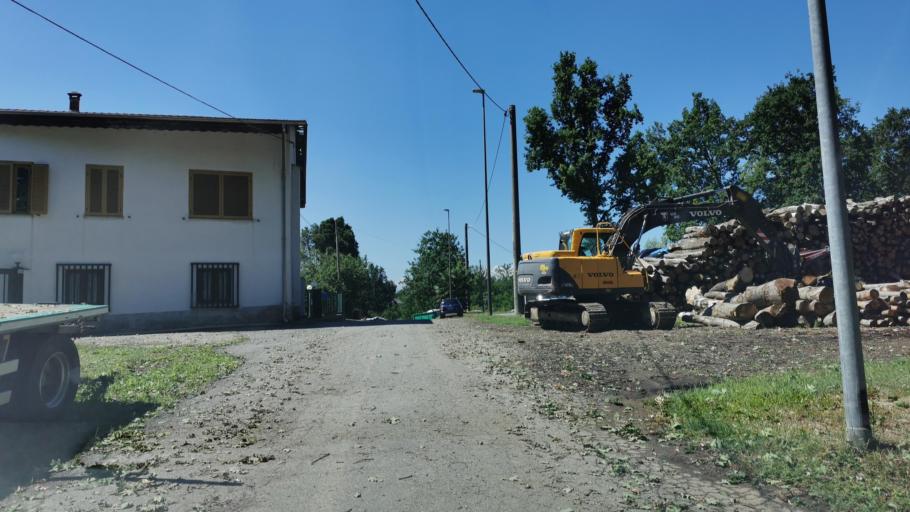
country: IT
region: Piedmont
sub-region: Provincia di Torino
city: San Francesco al Campo
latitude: 45.2423
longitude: 7.6679
